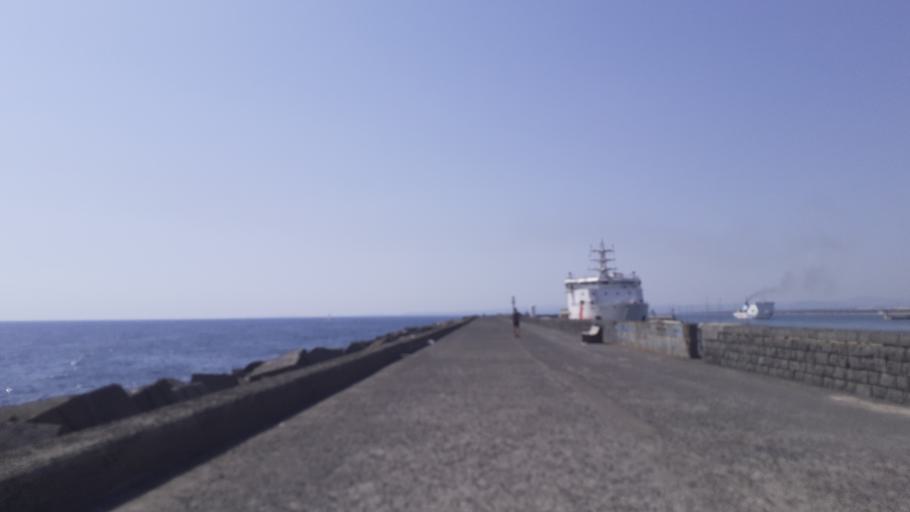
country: IT
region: Sicily
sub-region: Catania
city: Catania
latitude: 37.4958
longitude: 15.0995
